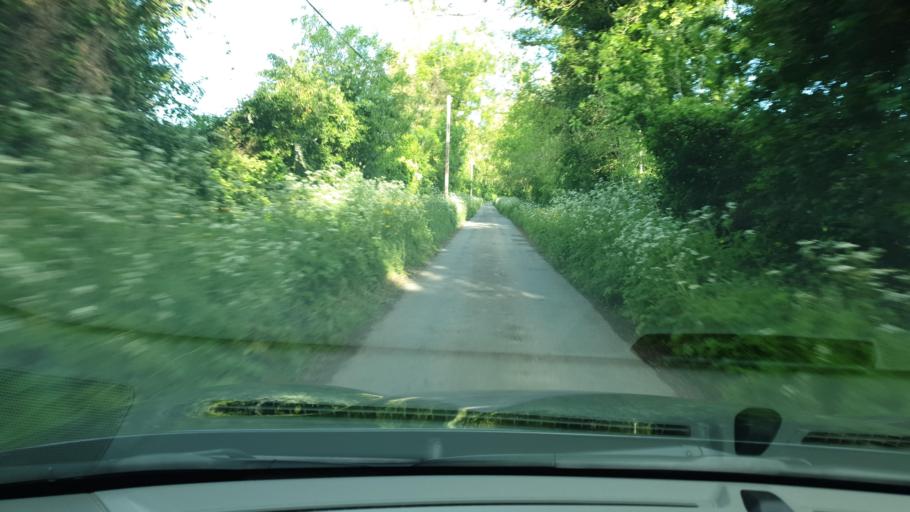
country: IE
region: Leinster
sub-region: An Mhi
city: Ashbourne
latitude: 53.5498
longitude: -6.4175
